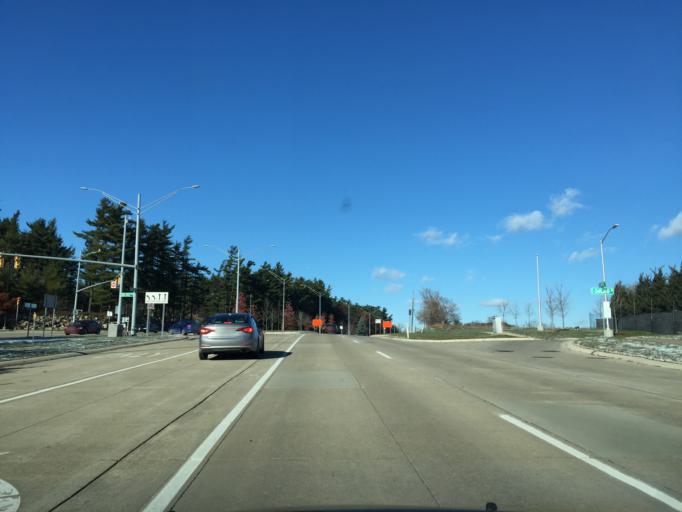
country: US
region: Michigan
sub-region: Oakland County
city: Auburn Hills
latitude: 42.6655
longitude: -83.2194
